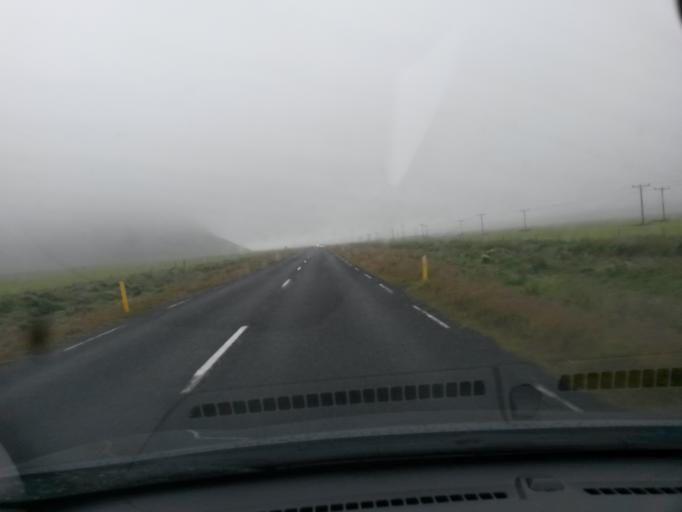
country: IS
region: South
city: Vestmannaeyjar
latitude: 63.4660
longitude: -19.2406
